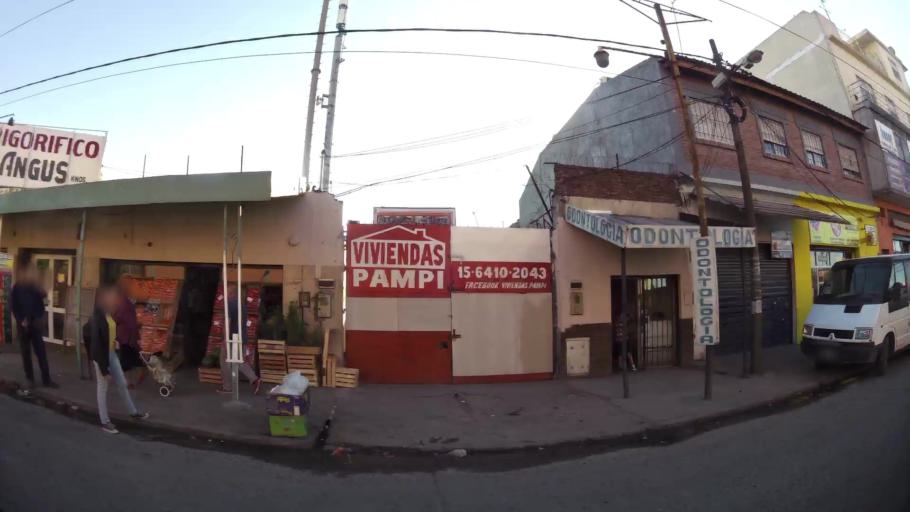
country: AR
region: Buenos Aires
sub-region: Partido de Almirante Brown
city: Adrogue
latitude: -34.7509
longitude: -58.3391
